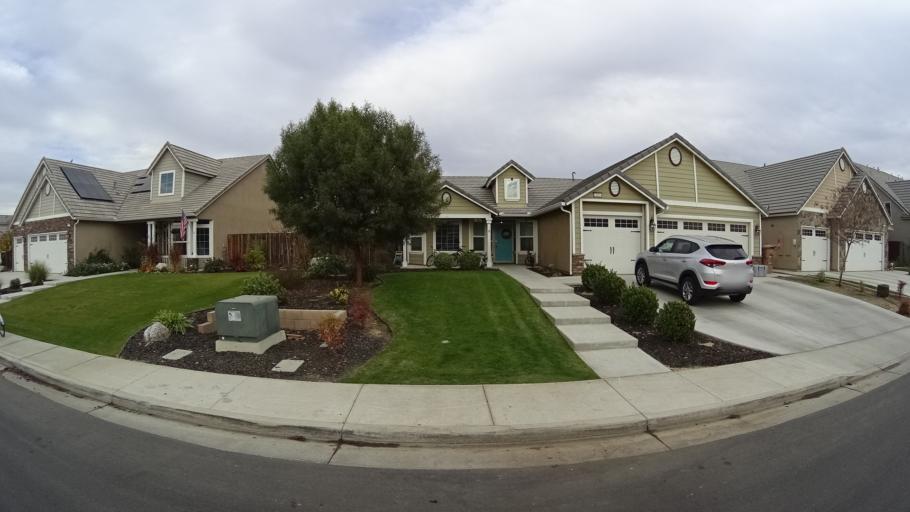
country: US
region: California
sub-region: Kern County
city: Rosedale
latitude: 35.4091
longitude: -119.1536
